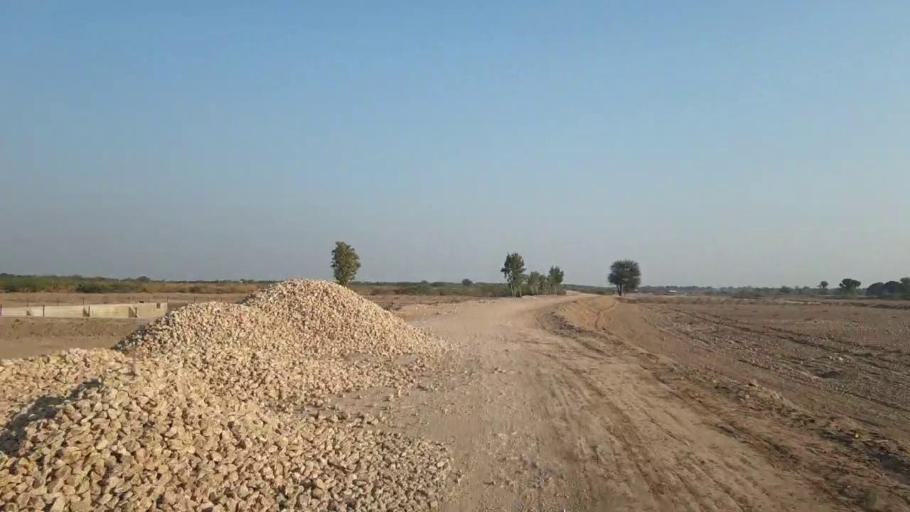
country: PK
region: Sindh
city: Mirpur Khas
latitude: 25.4275
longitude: 68.9005
